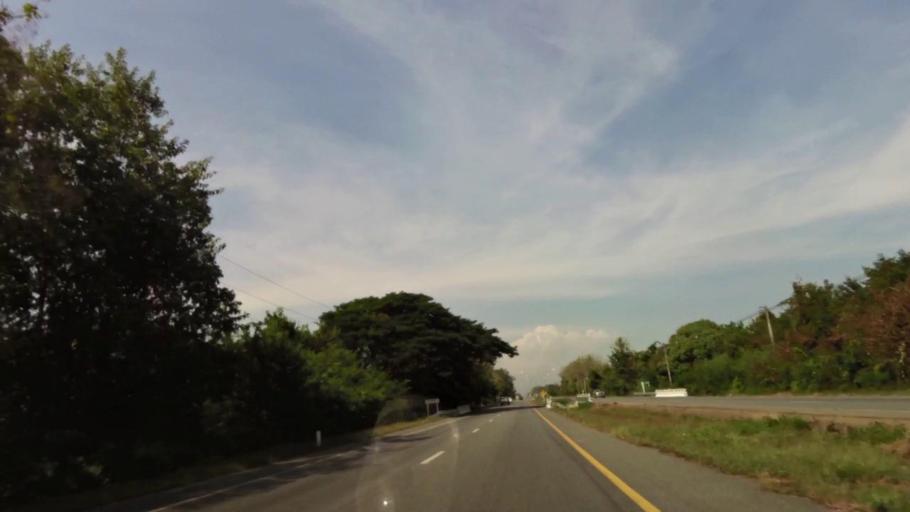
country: TH
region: Uttaradit
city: Tron
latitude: 17.5400
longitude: 100.1984
